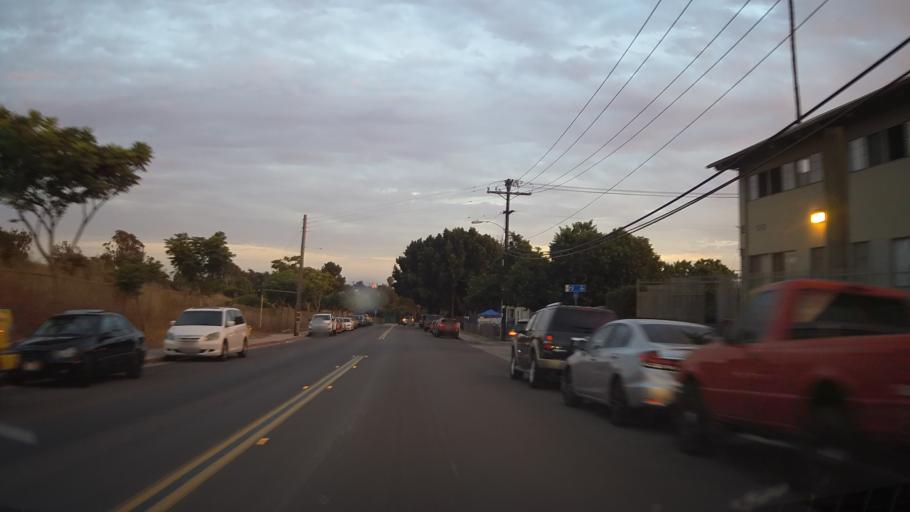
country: US
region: California
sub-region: San Diego County
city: National City
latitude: 32.7098
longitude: -117.1166
